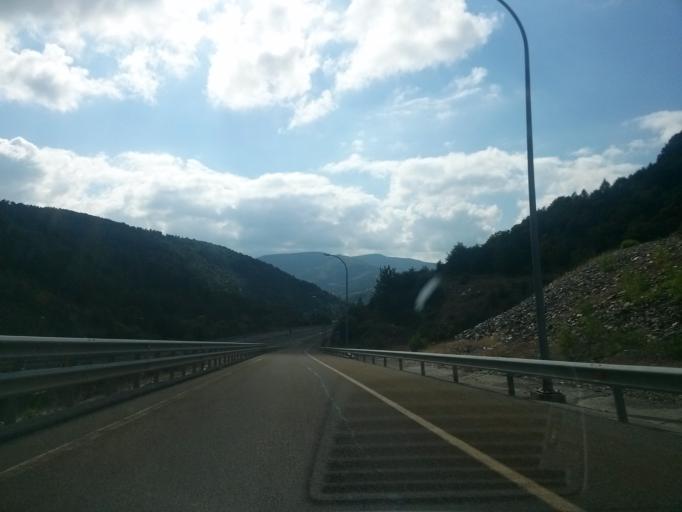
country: ES
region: Castille and Leon
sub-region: Provincia de Leon
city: Balboa
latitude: 42.7266
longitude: -7.0307
